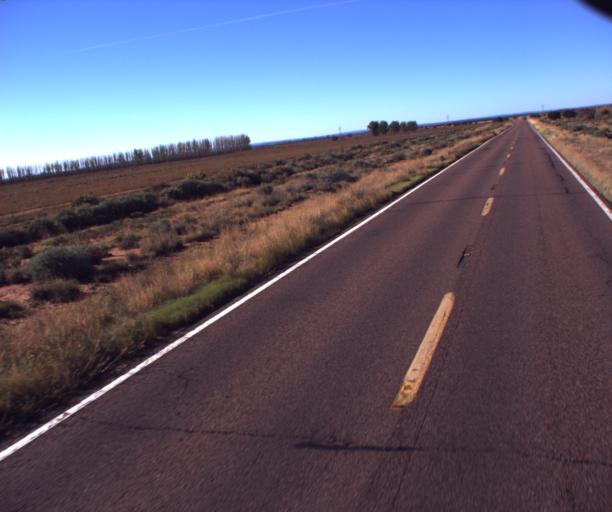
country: US
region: Arizona
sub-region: Navajo County
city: Heber-Overgaard
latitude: 34.6168
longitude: -110.3737
